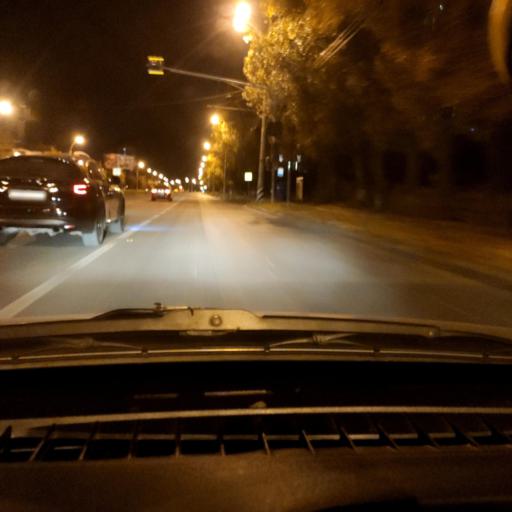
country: RU
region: Samara
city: Tol'yatti
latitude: 53.5154
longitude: 49.2576
